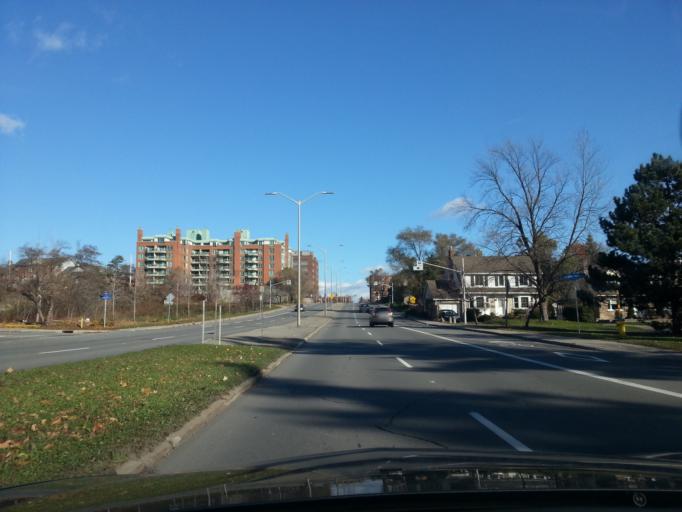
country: CA
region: Ontario
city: Ottawa
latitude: 45.3993
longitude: -75.7036
